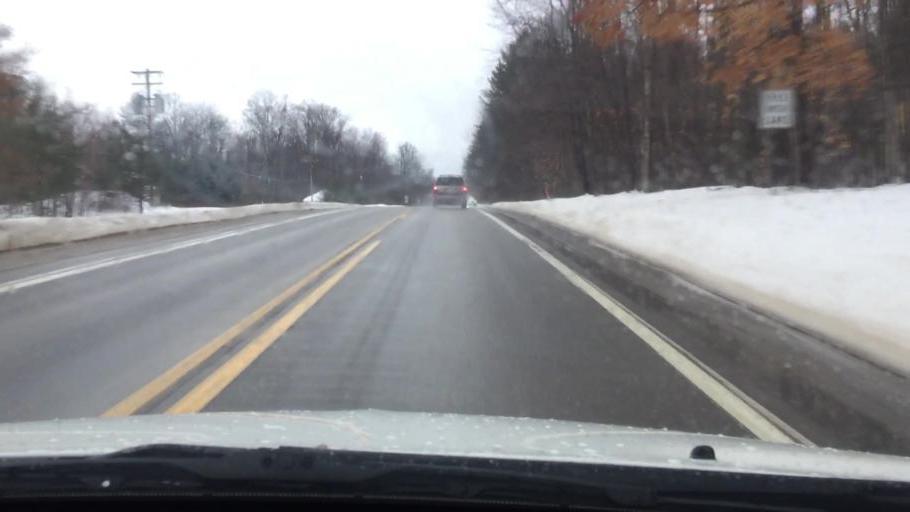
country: US
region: Michigan
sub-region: Charlevoix County
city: East Jordan
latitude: 45.2044
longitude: -85.1652
